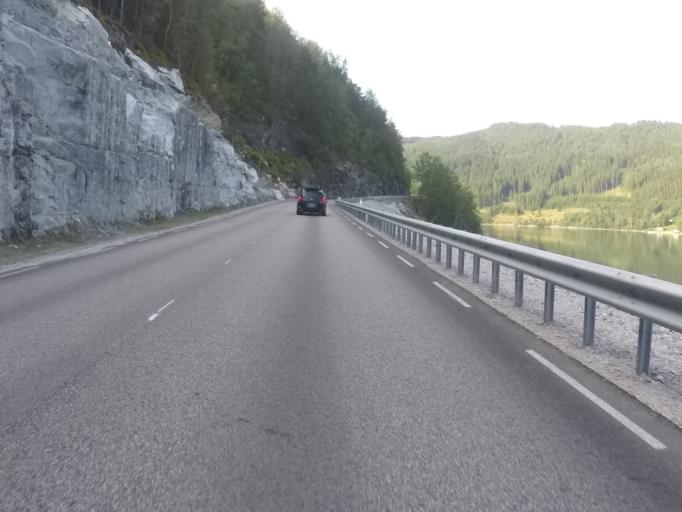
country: NO
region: More og Romsdal
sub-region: Rauma
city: Andalsnes
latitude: 62.5798
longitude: 7.5431
